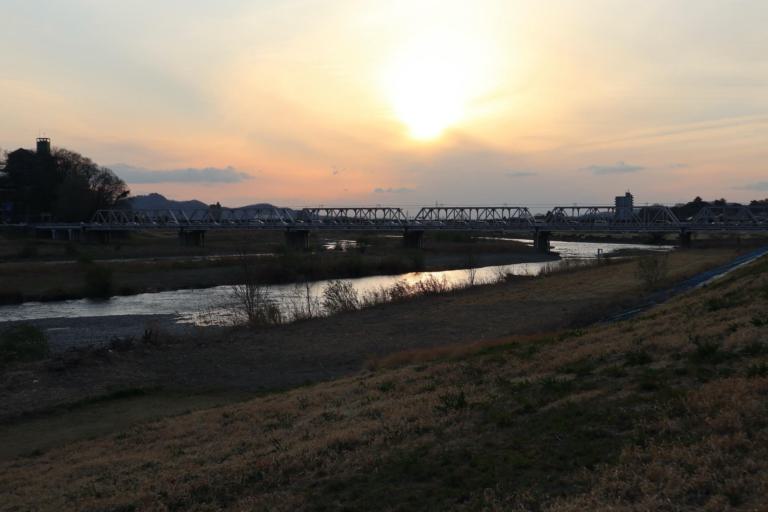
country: JP
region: Tochigi
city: Ashikaga
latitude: 36.3350
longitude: 139.4476
